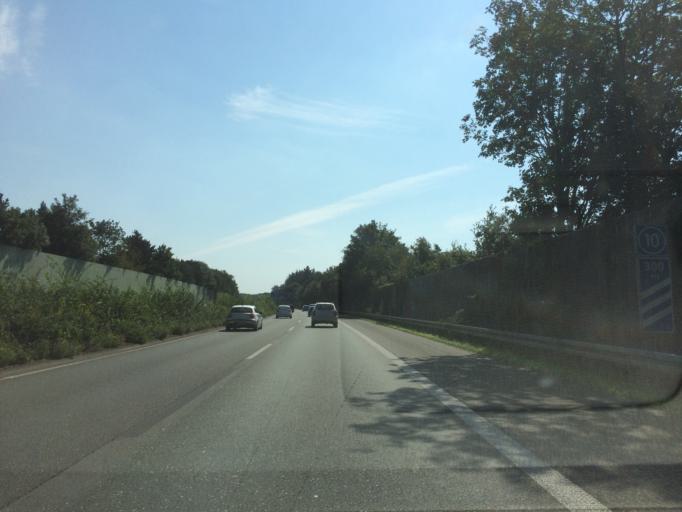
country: DE
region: North Rhine-Westphalia
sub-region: Regierungsbezirk Munster
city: Recklinghausen
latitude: 51.6611
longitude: 7.1595
